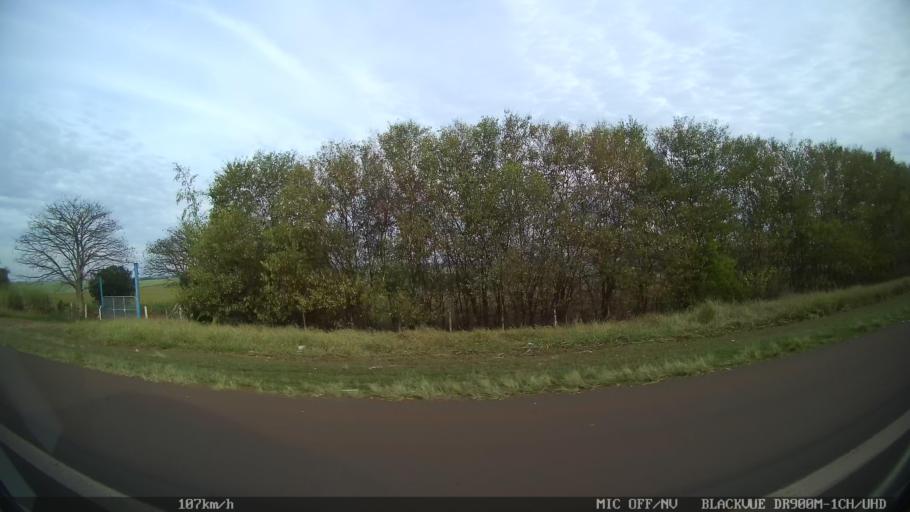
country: BR
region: Sao Paulo
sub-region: Iracemapolis
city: Iracemapolis
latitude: -22.6693
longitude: -47.5419
